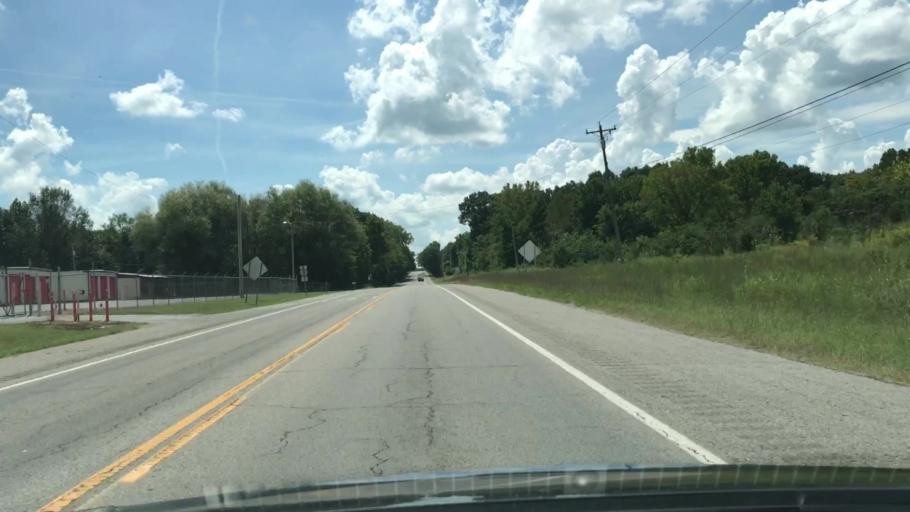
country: US
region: Tennessee
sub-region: Sumner County
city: White House
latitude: 36.5259
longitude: -86.6376
